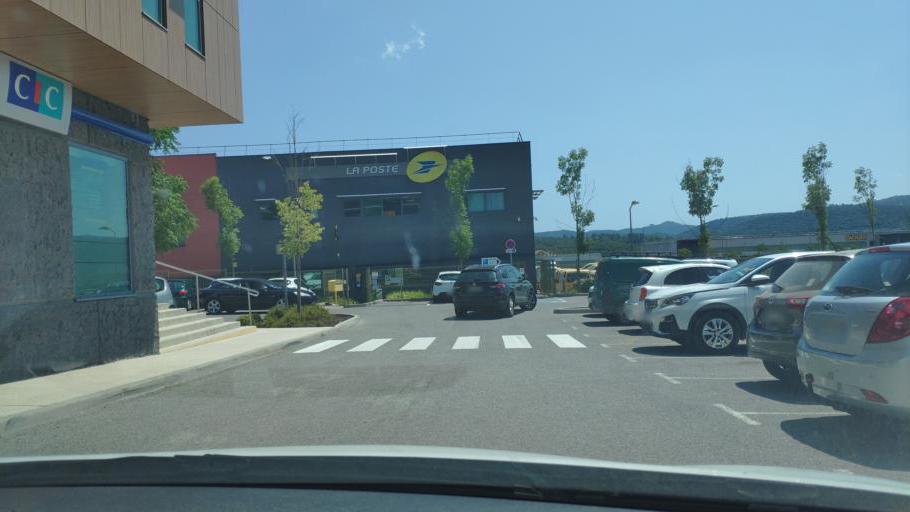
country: FR
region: Provence-Alpes-Cote d'Azur
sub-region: Departement du Var
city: Les Arcs
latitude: 43.4540
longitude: 6.4914
